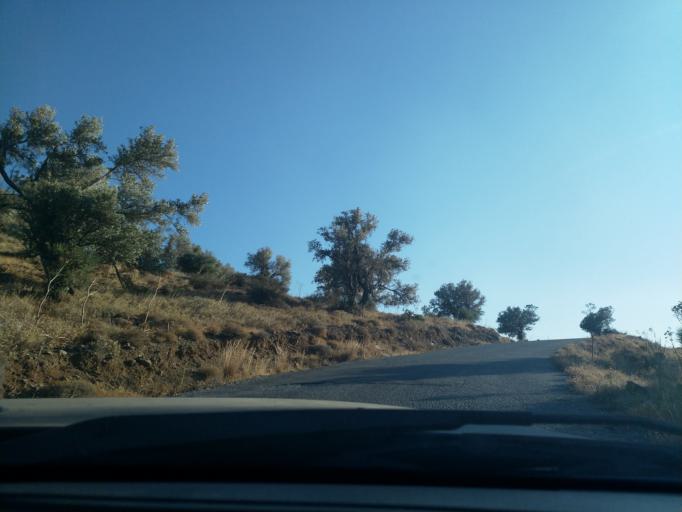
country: GR
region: Crete
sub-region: Nomos Rethymnis
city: Agia Galini
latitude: 35.1122
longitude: 24.5666
